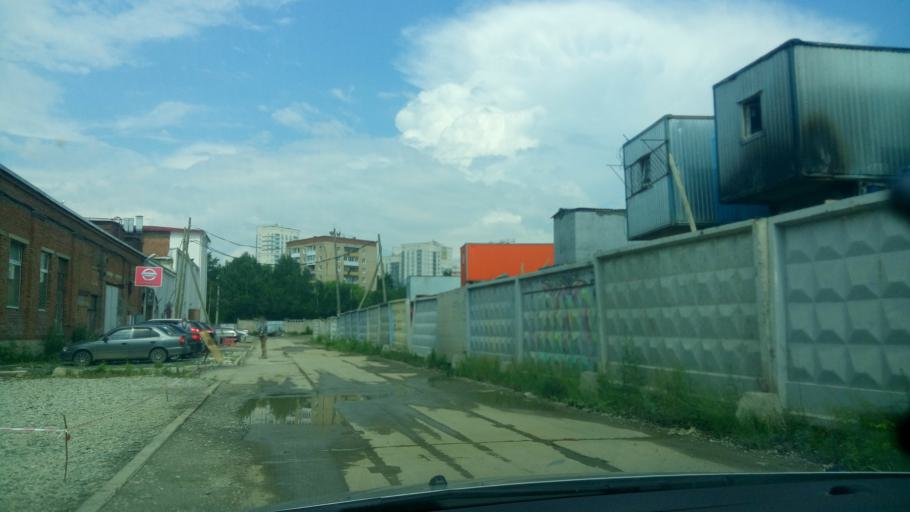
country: RU
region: Sverdlovsk
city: Yekaterinburg
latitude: 56.8583
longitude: 60.6599
